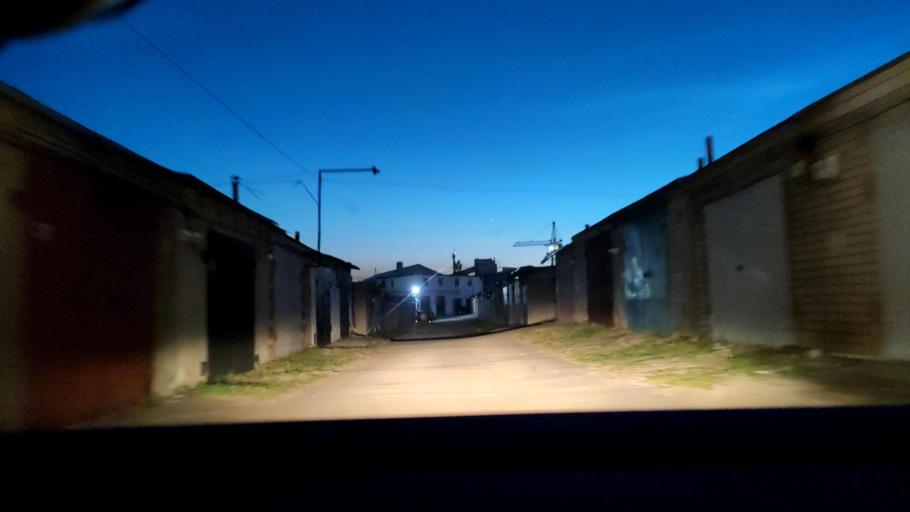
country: RU
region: Voronezj
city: Podgornoye
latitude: 51.7081
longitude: 39.1327
